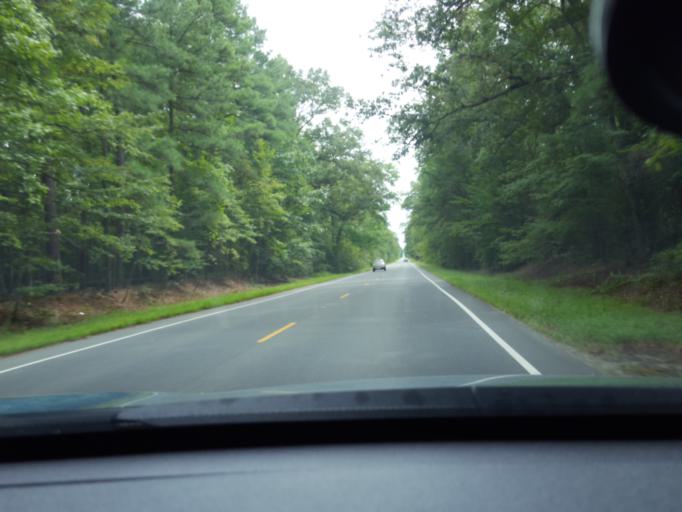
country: US
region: Virginia
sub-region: Caroline County
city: Bowling Green
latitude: 37.9740
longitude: -77.3408
